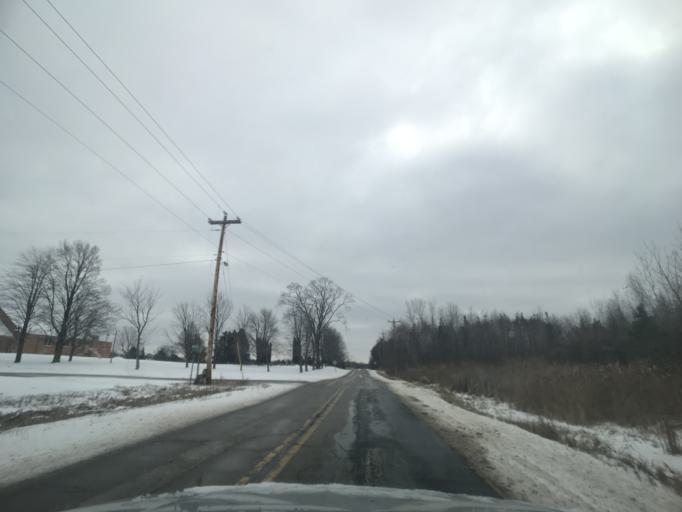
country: US
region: Wisconsin
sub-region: Brown County
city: Suamico
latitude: 44.7200
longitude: -88.0709
